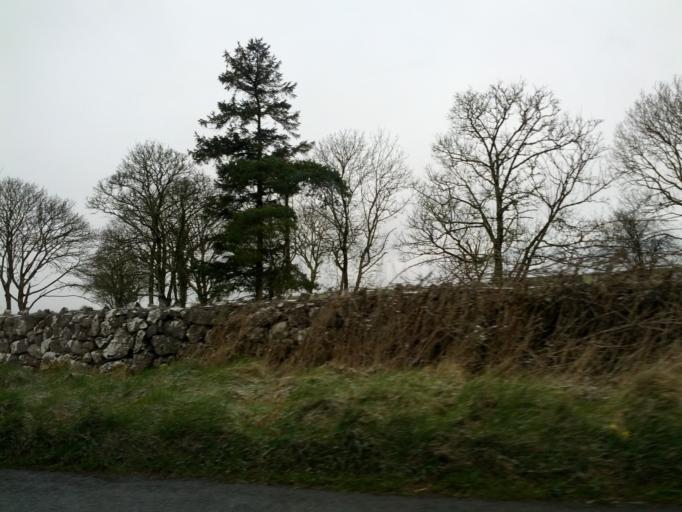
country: IE
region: Connaught
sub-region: County Galway
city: Oranmore
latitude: 53.2612
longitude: -8.8294
